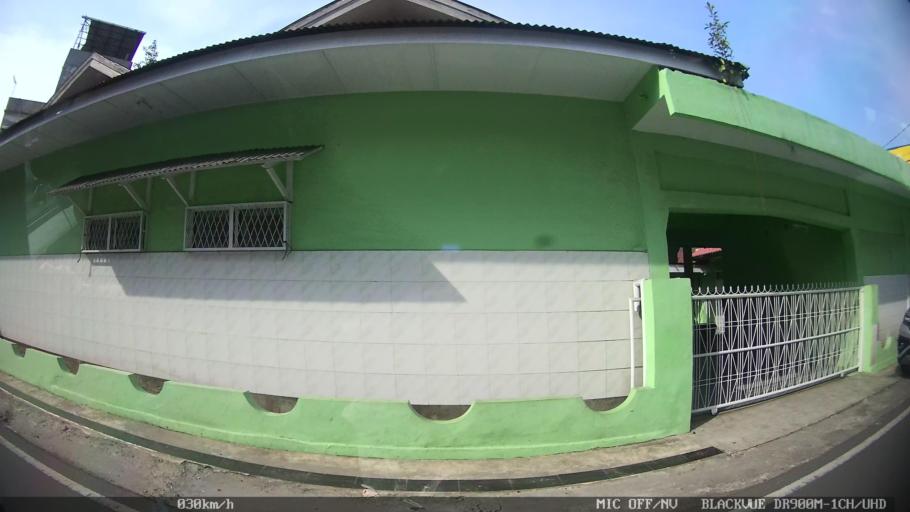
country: ID
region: North Sumatra
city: Binjai
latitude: 3.6044
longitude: 98.4870
